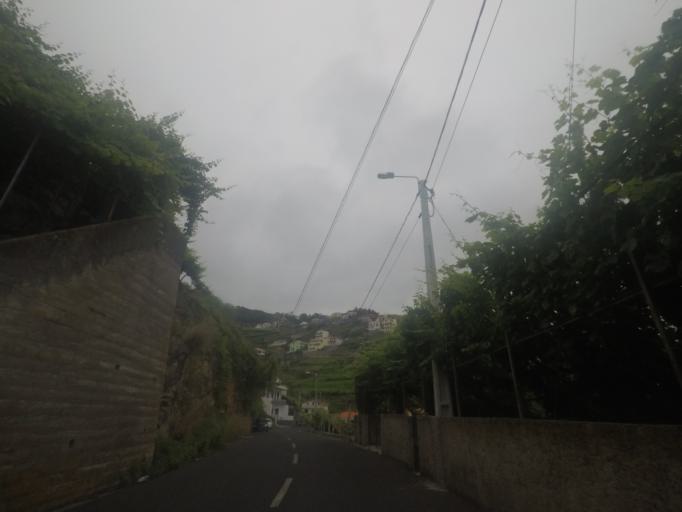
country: PT
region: Madeira
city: Camara de Lobos
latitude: 32.6722
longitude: -16.9721
